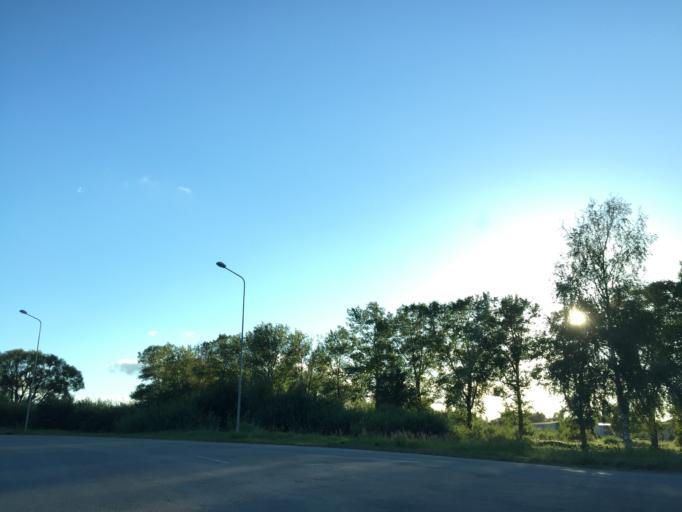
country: LV
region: Kuldigas Rajons
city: Kuldiga
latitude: 56.9580
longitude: 21.9873
